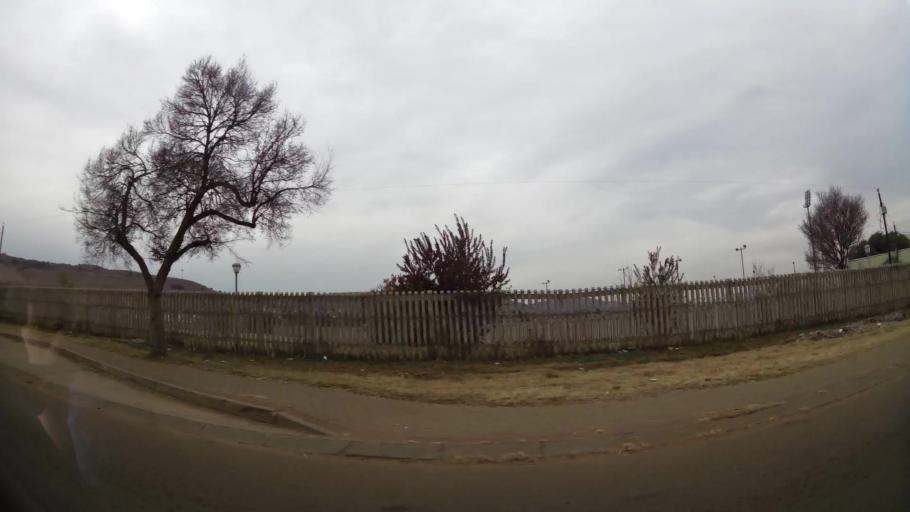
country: ZA
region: Gauteng
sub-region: City of Tshwane Metropolitan Municipality
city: Pretoria
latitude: -25.7065
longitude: 28.3367
